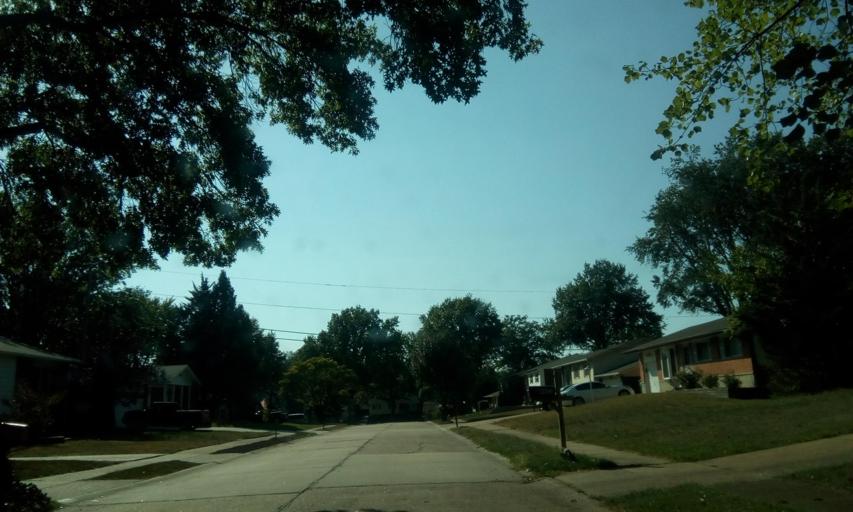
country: US
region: Missouri
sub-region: Saint Louis County
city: Mehlville
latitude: 38.4951
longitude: -90.3497
